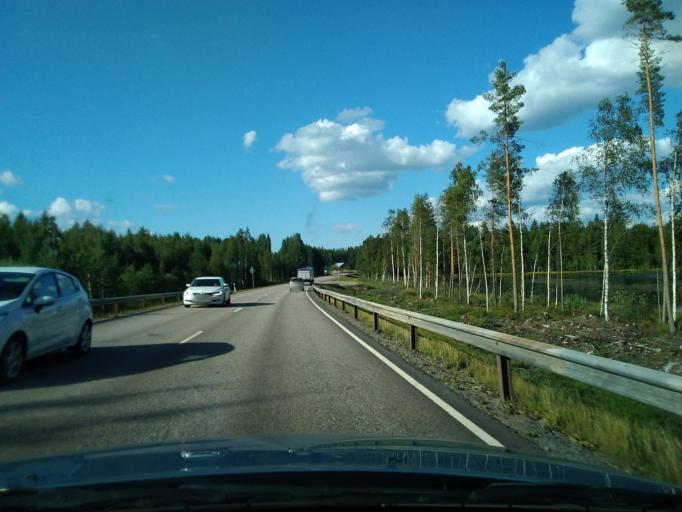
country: FI
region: Pirkanmaa
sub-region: Ylae-Pirkanmaa
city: Maenttae
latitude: 62.0929
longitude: 24.7278
